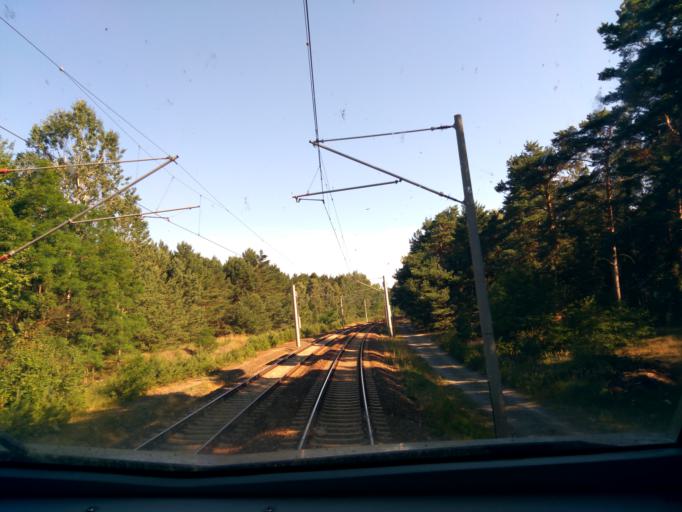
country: DE
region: Brandenburg
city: Bestensee
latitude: 52.2109
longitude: 13.6184
